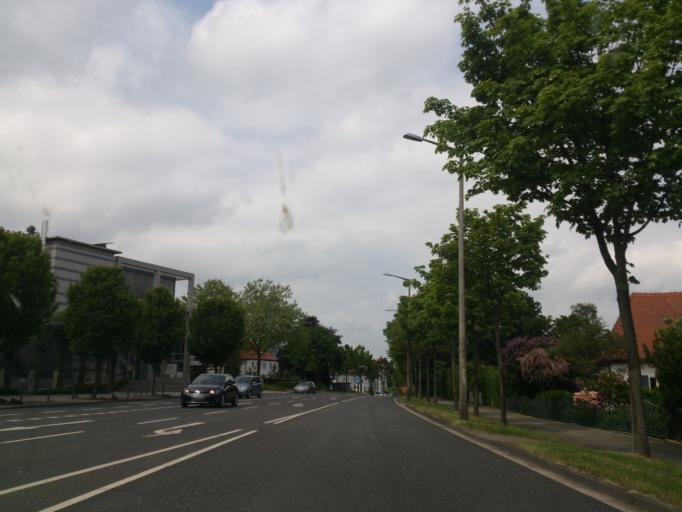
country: DE
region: Hesse
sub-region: Regierungsbezirk Kassel
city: Baunatal
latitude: 51.3043
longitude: 9.4263
